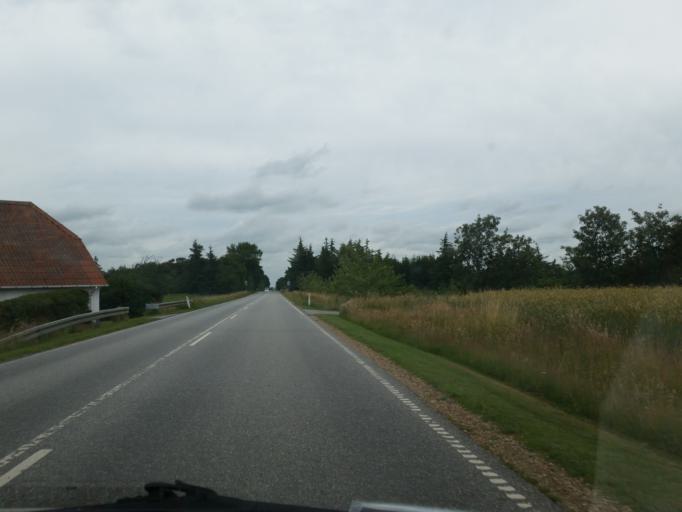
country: DK
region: South Denmark
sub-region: Esbjerg Kommune
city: Ribe
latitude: 55.3577
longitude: 8.7919
